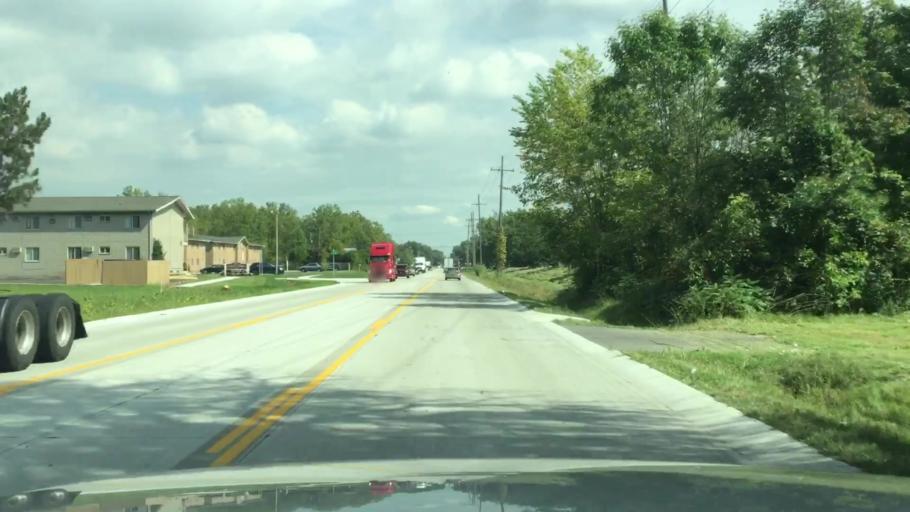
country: US
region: Michigan
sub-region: Wayne County
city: Wayne
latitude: 42.2527
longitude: -83.3552
